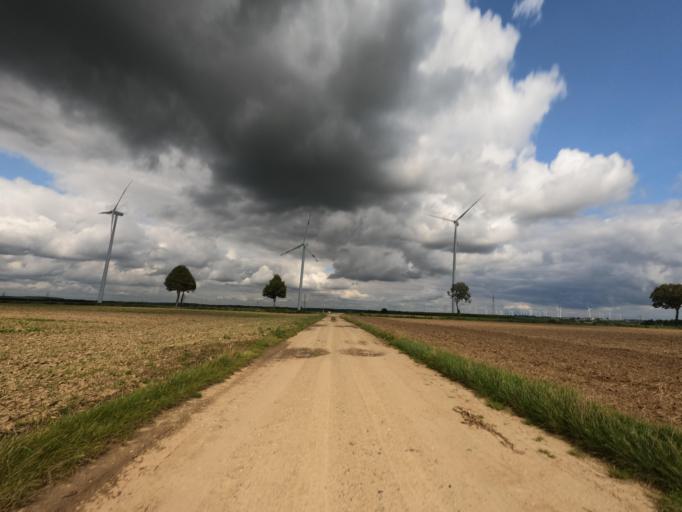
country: DE
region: North Rhine-Westphalia
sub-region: Regierungsbezirk Koln
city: Linnich
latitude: 50.9873
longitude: 6.2307
